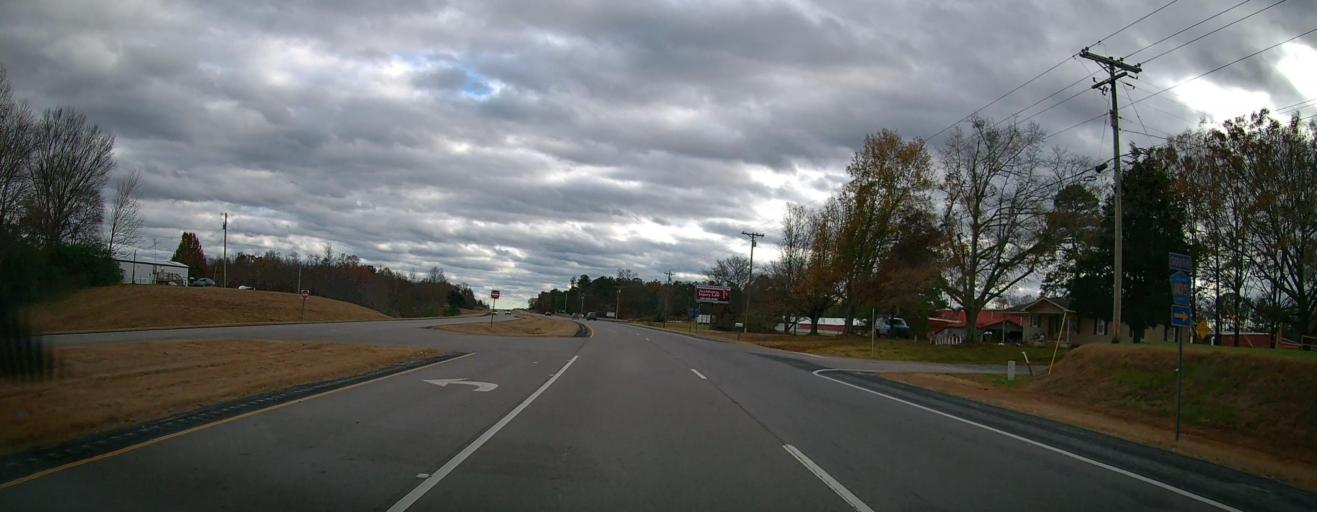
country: US
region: Alabama
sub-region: Morgan County
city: Falkville
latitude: 34.2866
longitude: -86.9980
